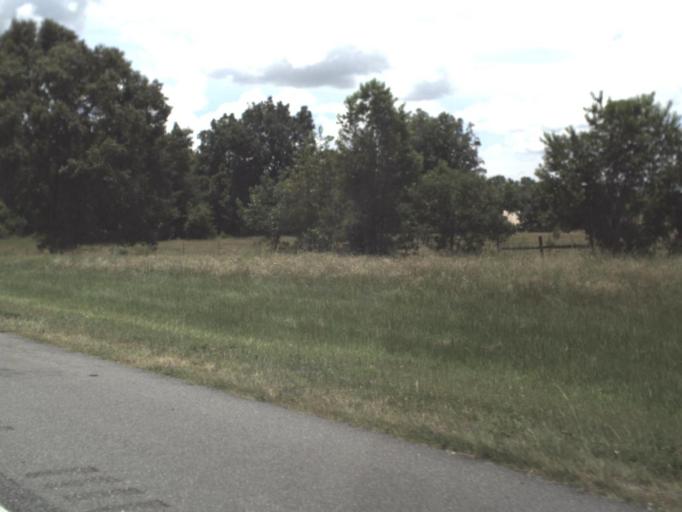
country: US
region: Florida
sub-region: Alachua County
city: High Springs
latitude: 29.9863
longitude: -82.5820
